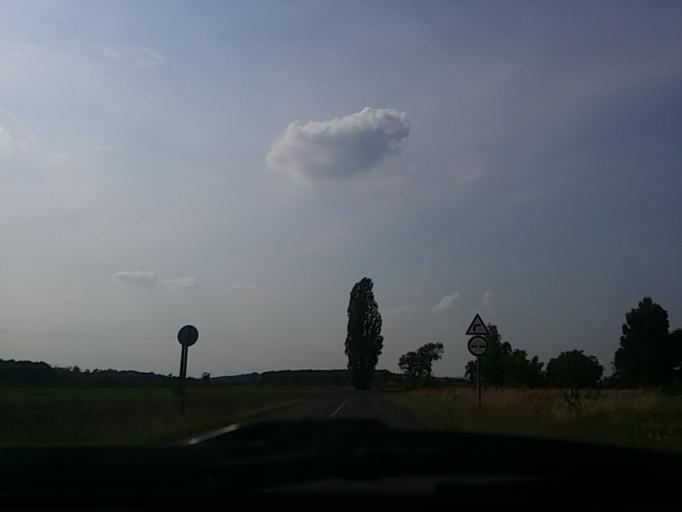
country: HU
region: Komarom-Esztergom
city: Oroszlany
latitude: 47.4959
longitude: 18.3717
